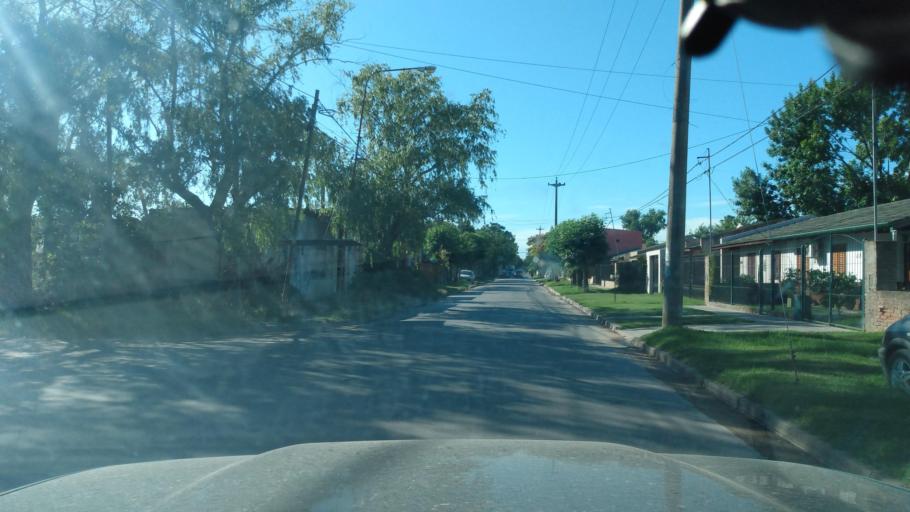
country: AR
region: Buenos Aires
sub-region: Partido de Lujan
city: Lujan
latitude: -34.5690
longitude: -59.0909
